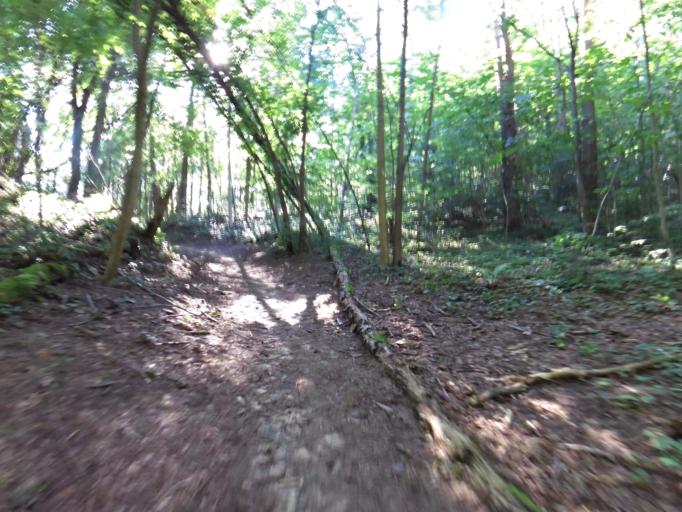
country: LT
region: Vilnius County
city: Justiniskes
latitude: 54.6900
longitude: 25.2251
